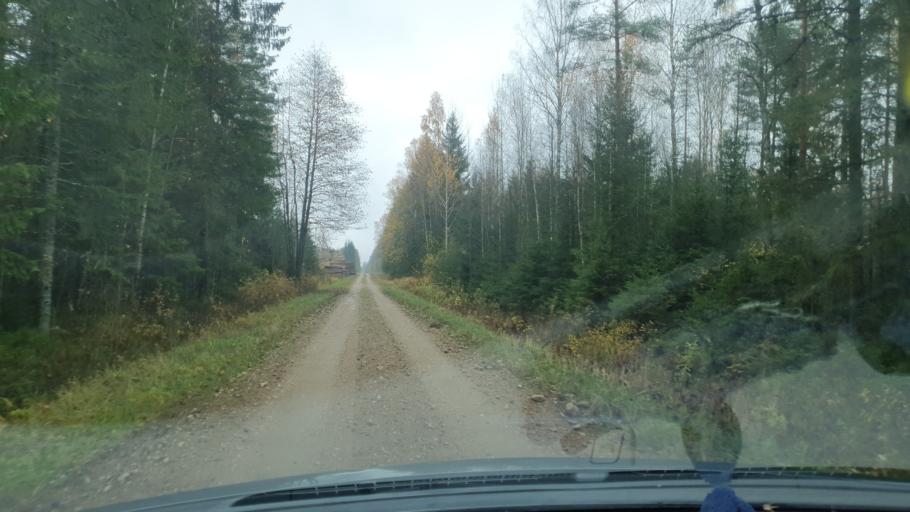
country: EE
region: Viljandimaa
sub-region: Karksi vald
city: Karksi-Nuia
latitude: 57.9801
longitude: 25.6285
